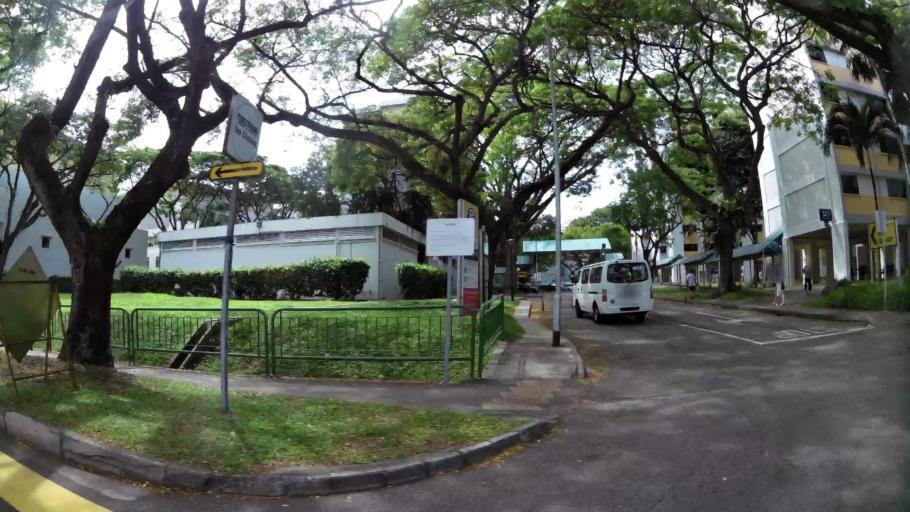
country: SG
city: Singapore
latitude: 1.3168
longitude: 103.7669
